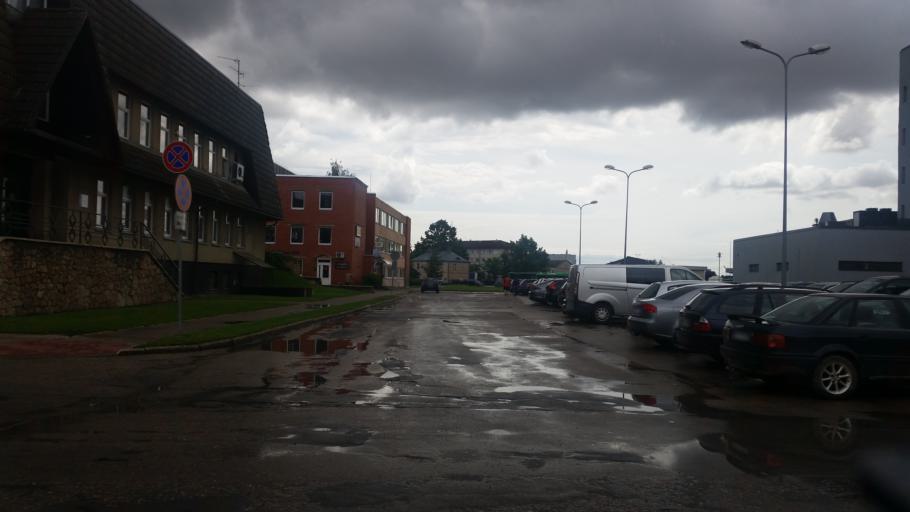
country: LV
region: Bauskas Rajons
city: Bauska
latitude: 56.4084
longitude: 24.1961
